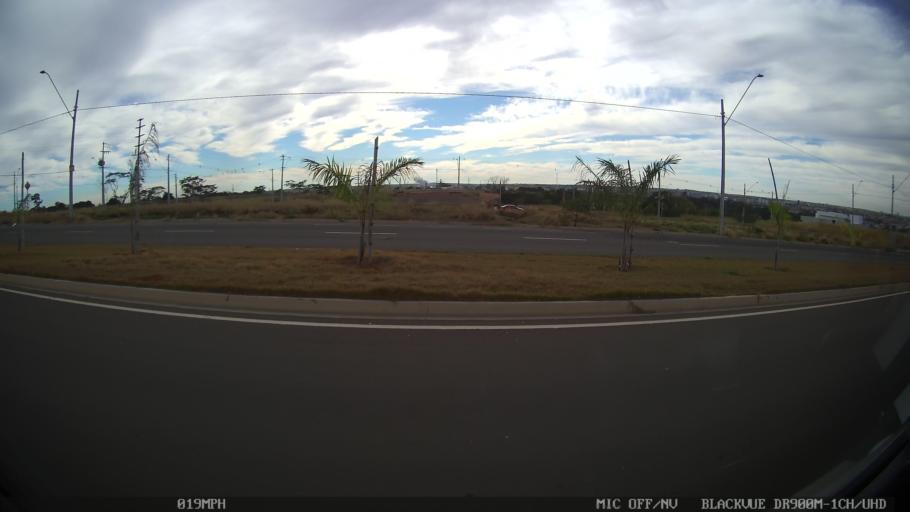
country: BR
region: Sao Paulo
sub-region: Catanduva
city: Catanduva
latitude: -21.1357
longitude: -49.0142
